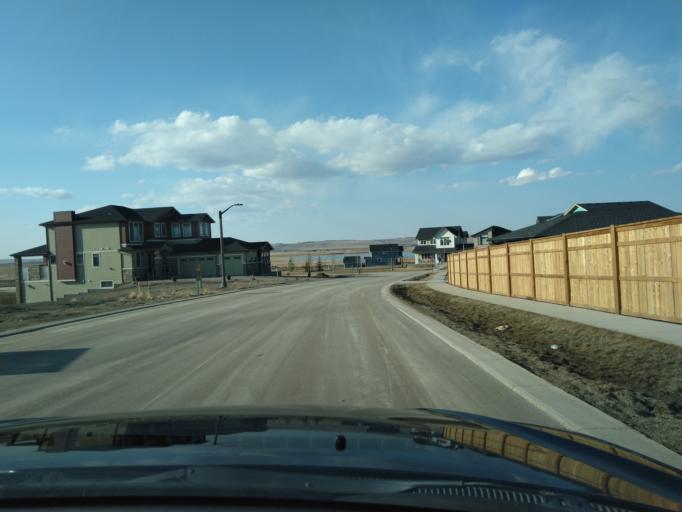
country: CA
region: Alberta
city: Cochrane
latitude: 51.1115
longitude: -114.4045
